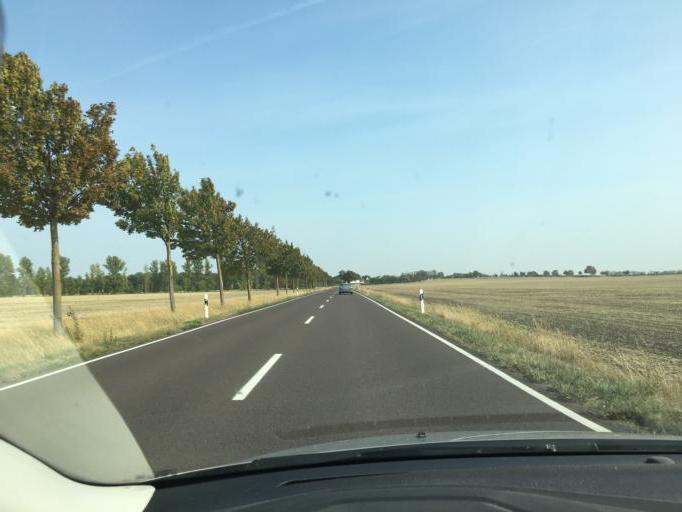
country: DE
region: Saxony-Anhalt
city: Wulfen
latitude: 51.7798
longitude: 11.8953
